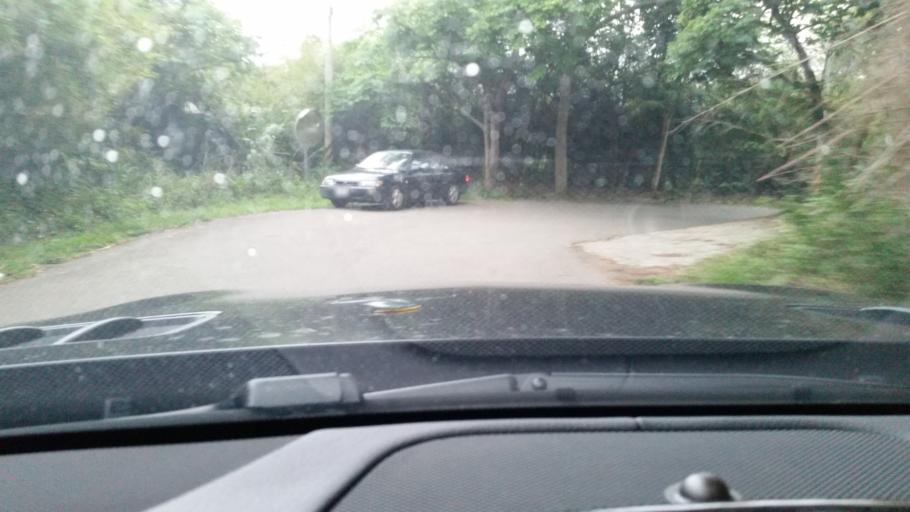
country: TW
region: Taiwan
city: Fengyuan
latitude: 24.3475
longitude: 120.7796
